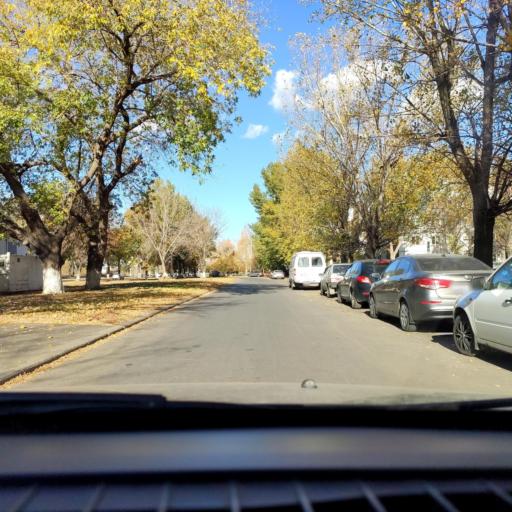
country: RU
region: Samara
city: Tol'yatti
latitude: 53.5144
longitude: 49.2582
